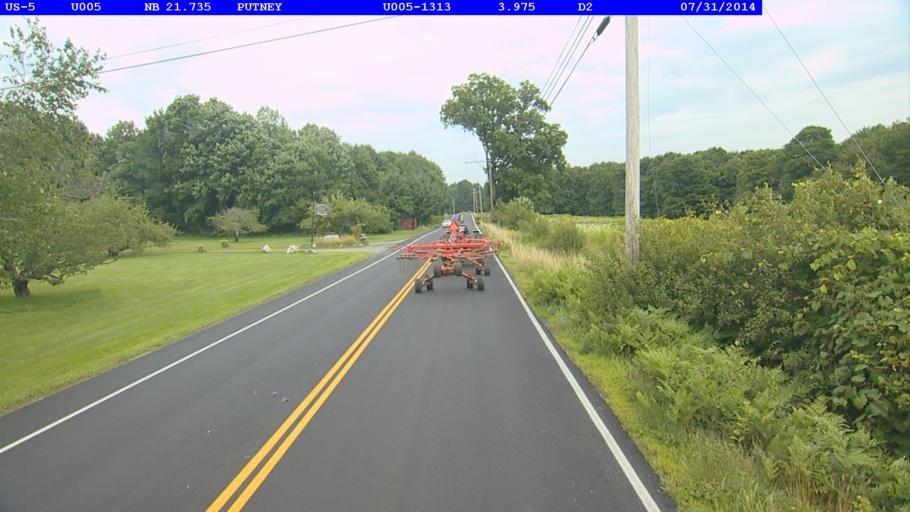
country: US
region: New Hampshire
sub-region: Cheshire County
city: Westmoreland
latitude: 42.9989
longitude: -72.4760
